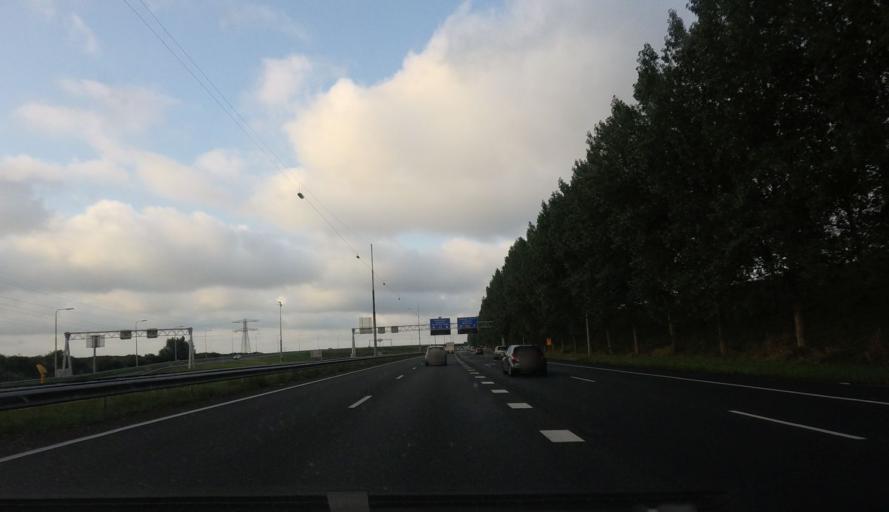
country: NL
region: North Holland
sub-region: Gemeente Heemskerk
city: Heemskerk
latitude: 52.4891
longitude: 4.6948
